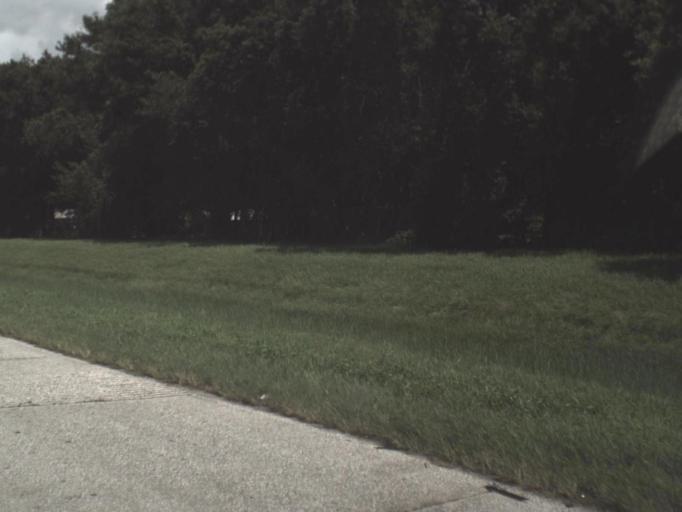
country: US
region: Florida
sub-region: Hillsborough County
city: Mango
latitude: 27.9578
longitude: -82.3269
